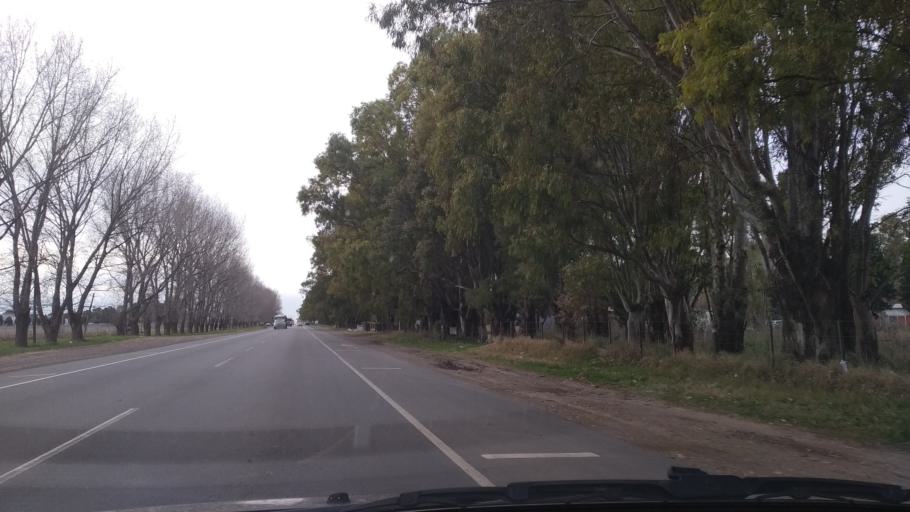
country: AR
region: Buenos Aires
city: Olavarria
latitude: -36.9685
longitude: -60.2702
